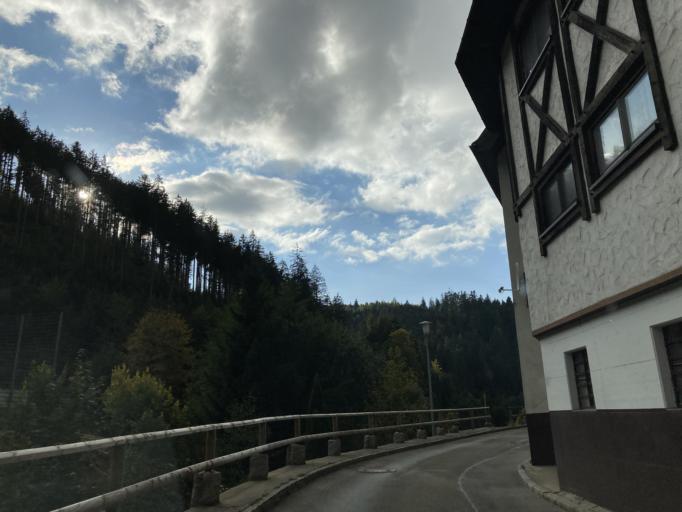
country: DE
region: Baden-Wuerttemberg
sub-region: Freiburg Region
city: Triberg im Schwarzwald
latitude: 48.1318
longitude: 8.2544
